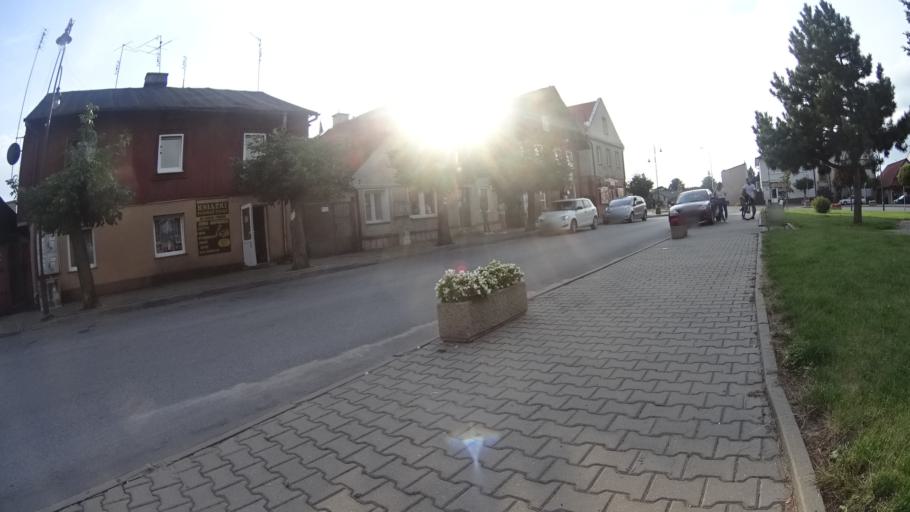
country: PL
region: Masovian Voivodeship
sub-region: Powiat grojecki
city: Mogielnica
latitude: 51.6935
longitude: 20.7230
